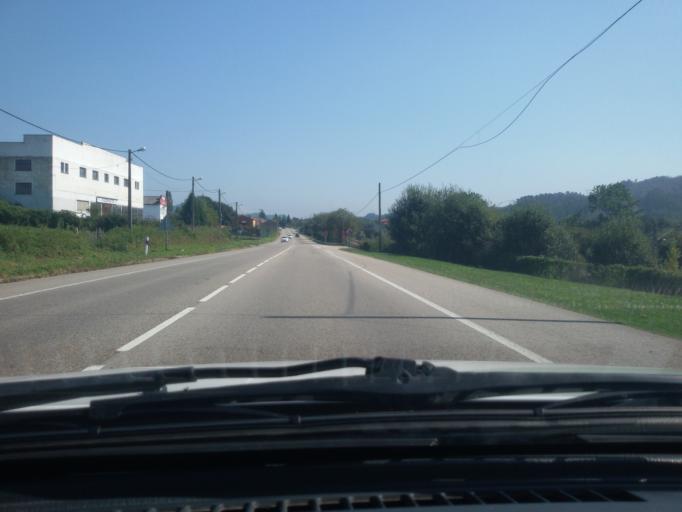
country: ES
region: Asturias
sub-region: Province of Asturias
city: Pola de Siero
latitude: 43.3871
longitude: -5.6851
